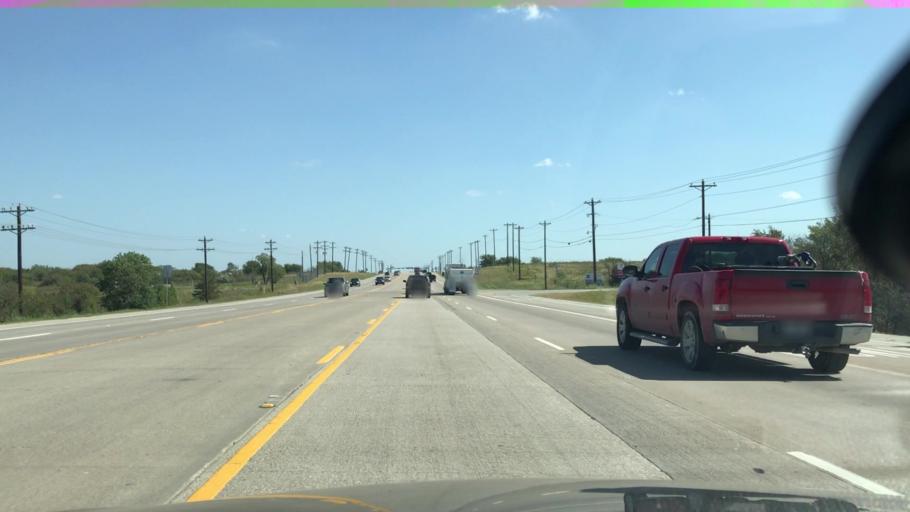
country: US
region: Texas
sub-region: Denton County
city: Little Elm
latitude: 33.2193
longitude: -96.8888
